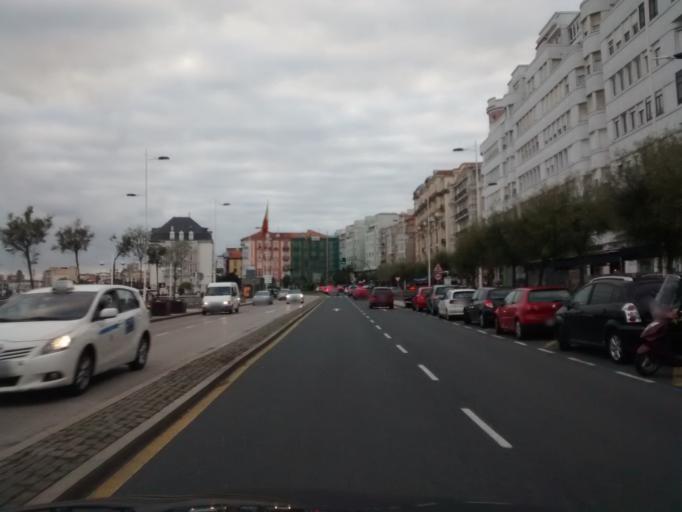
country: ES
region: Cantabria
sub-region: Provincia de Cantabria
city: Santander
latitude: 43.4630
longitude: -3.7942
